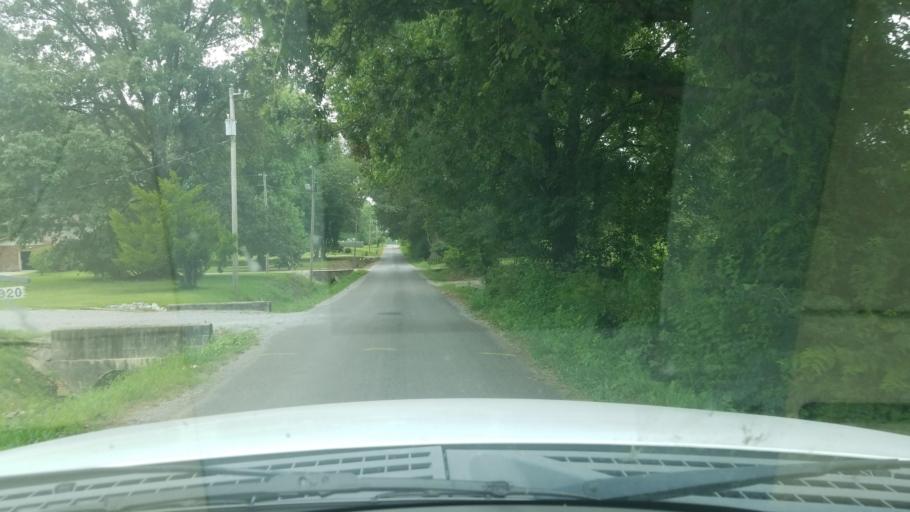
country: US
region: Illinois
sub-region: Saline County
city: Eldorado
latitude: 37.8300
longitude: -88.4478
